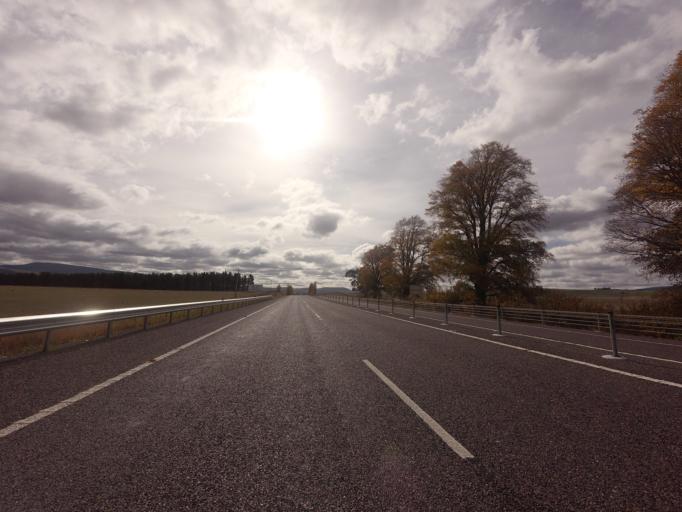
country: AU
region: Tasmania
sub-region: Brighton
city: Bridgewater
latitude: -42.5103
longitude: 147.1888
